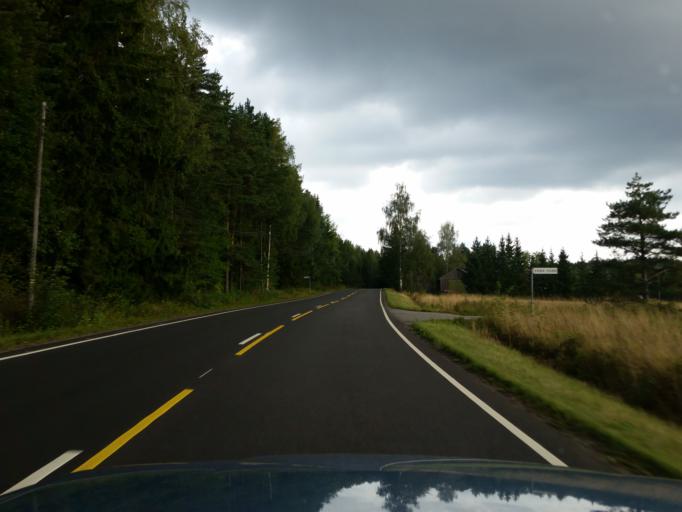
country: FI
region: Varsinais-Suomi
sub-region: Aboland-Turunmaa
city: Laensi-Turunmaa
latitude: 60.2663
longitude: 22.2205
